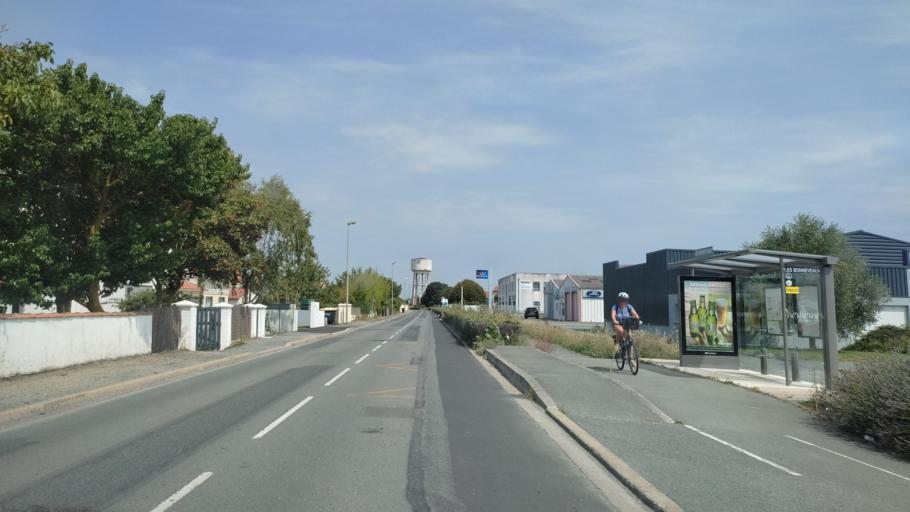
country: FR
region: Poitou-Charentes
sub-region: Departement de la Charente-Maritime
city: Chatelaillon-Plage
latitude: 46.0841
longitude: -1.0721
